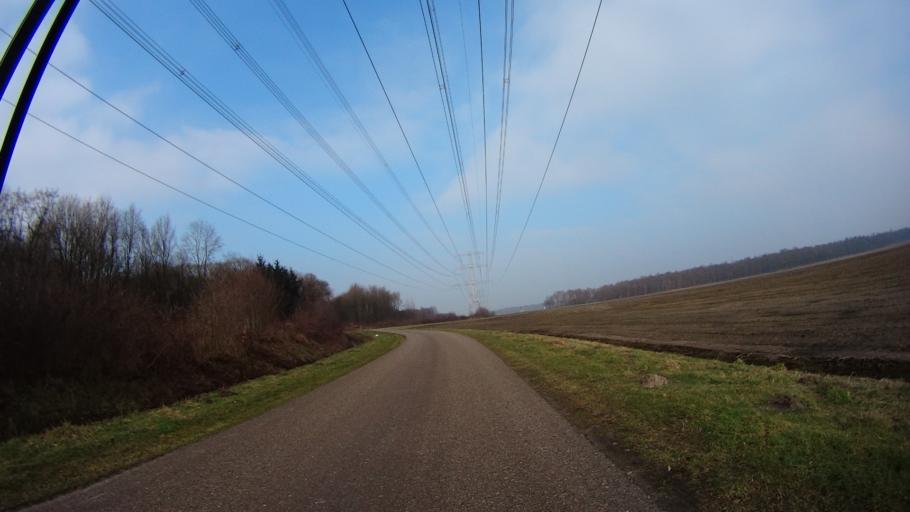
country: NL
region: Drenthe
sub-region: Gemeente Coevorden
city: Sleen
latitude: 52.7592
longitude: 6.8429
